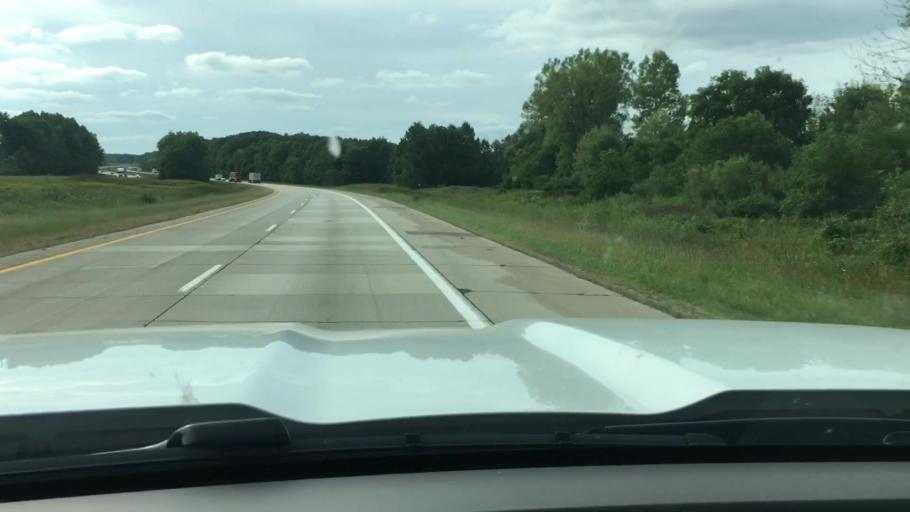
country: US
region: Michigan
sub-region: Lapeer County
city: Lapeer
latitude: 43.0094
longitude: -83.2257
